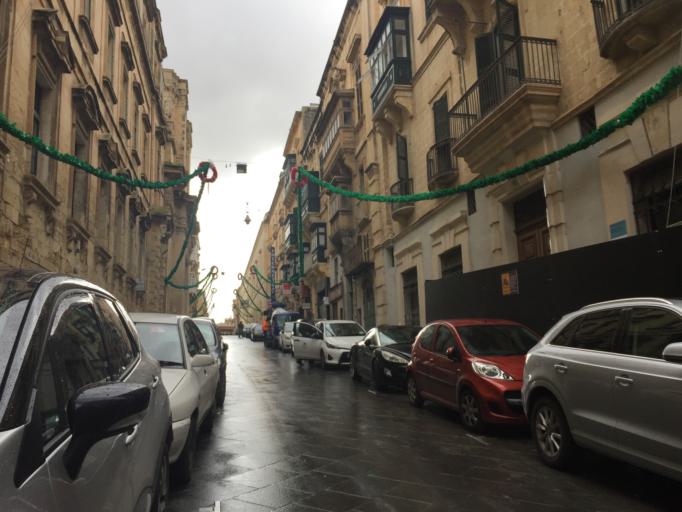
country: MT
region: Il-Belt Valletta
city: Valletta
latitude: 35.8991
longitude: 14.5159
